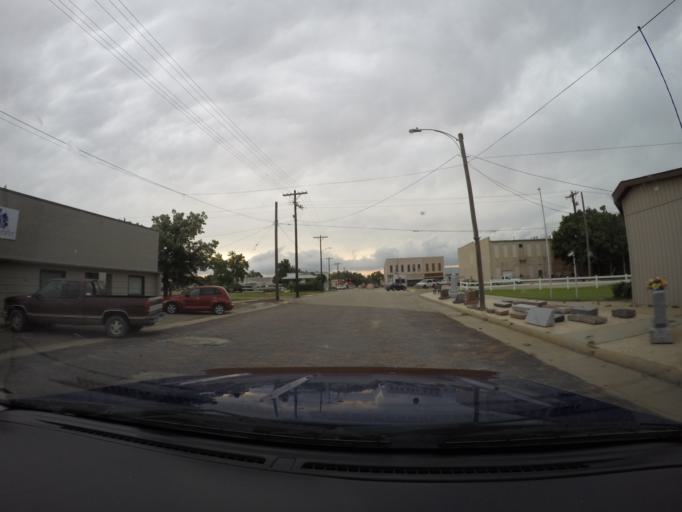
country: US
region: Kansas
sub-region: Clay County
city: Clay Center
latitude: 39.3754
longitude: -97.1284
